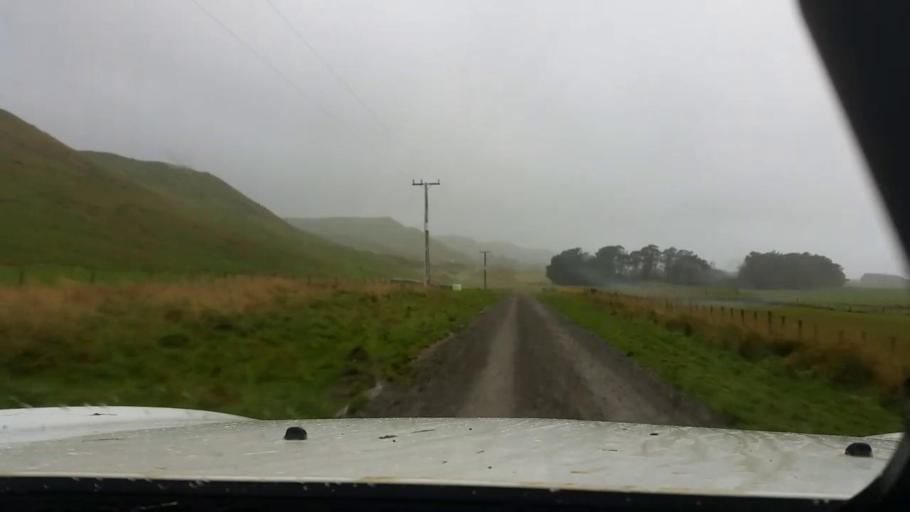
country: NZ
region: Wellington
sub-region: Masterton District
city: Masterton
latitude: -41.2552
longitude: 175.9082
